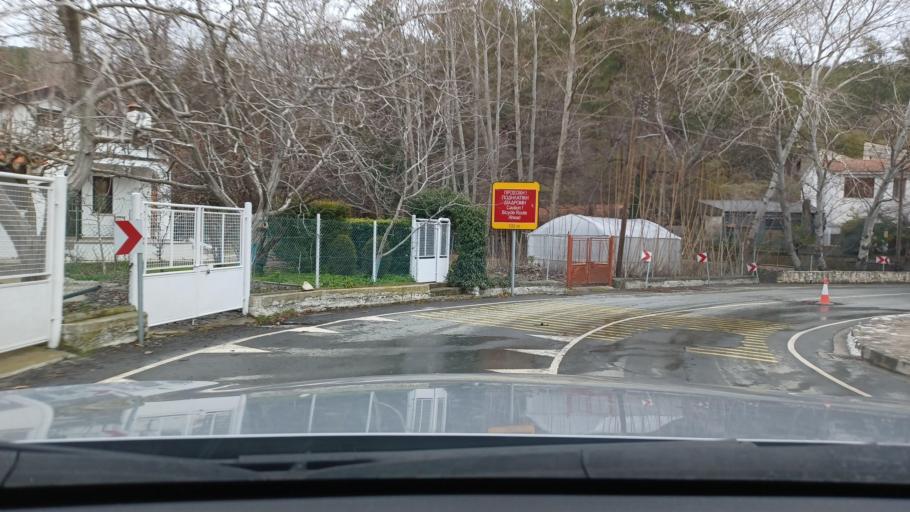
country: CY
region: Limassol
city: Pelendri
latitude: 34.8615
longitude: 32.8716
